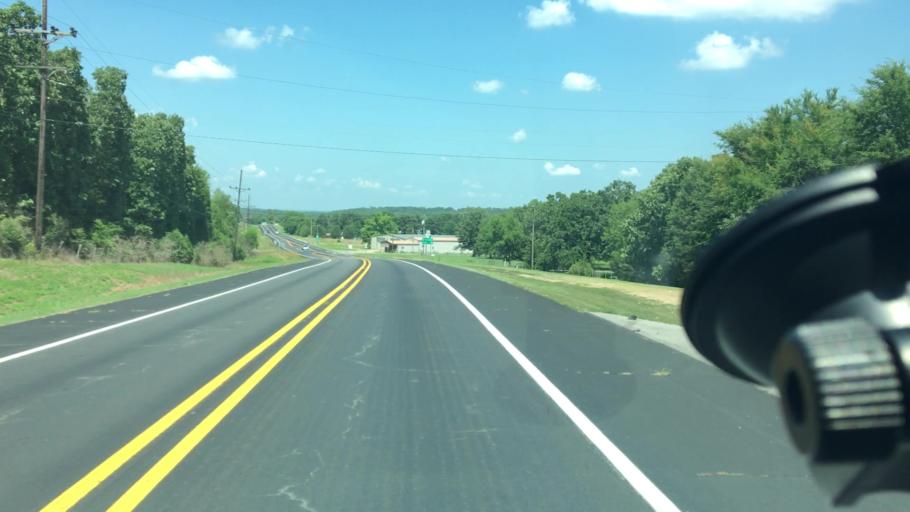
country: US
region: Arkansas
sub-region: Sebastian County
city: Lavaca
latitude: 35.3010
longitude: -94.1602
